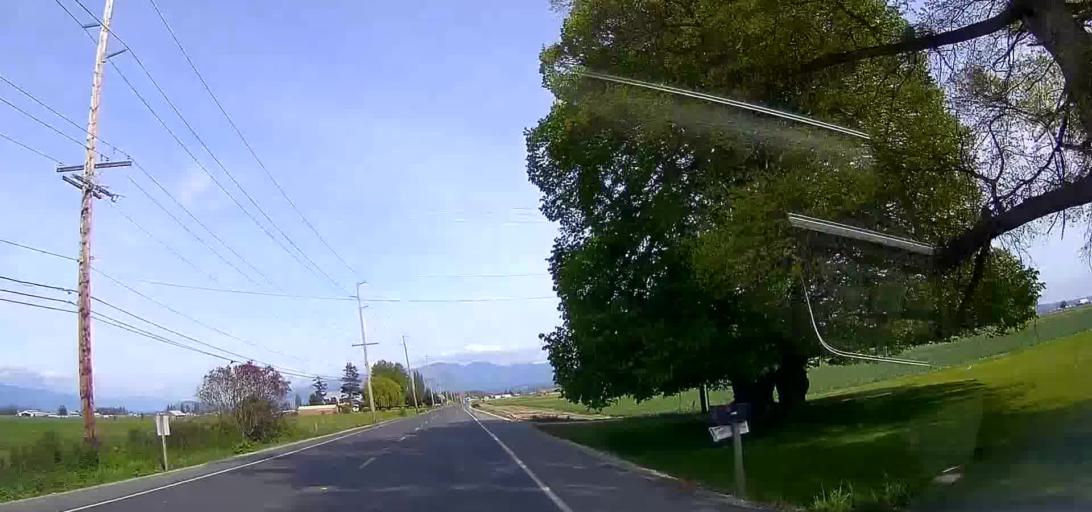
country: US
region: Washington
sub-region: Skagit County
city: Mount Vernon
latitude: 48.4209
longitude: -122.4644
